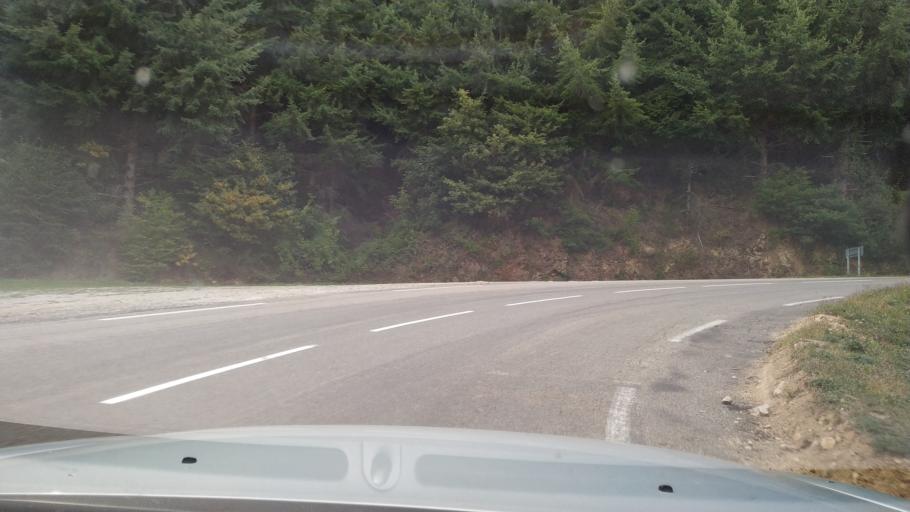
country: FR
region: Rhone-Alpes
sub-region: Departement de l'Ardeche
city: Desaignes
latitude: 44.9987
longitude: 4.4988
